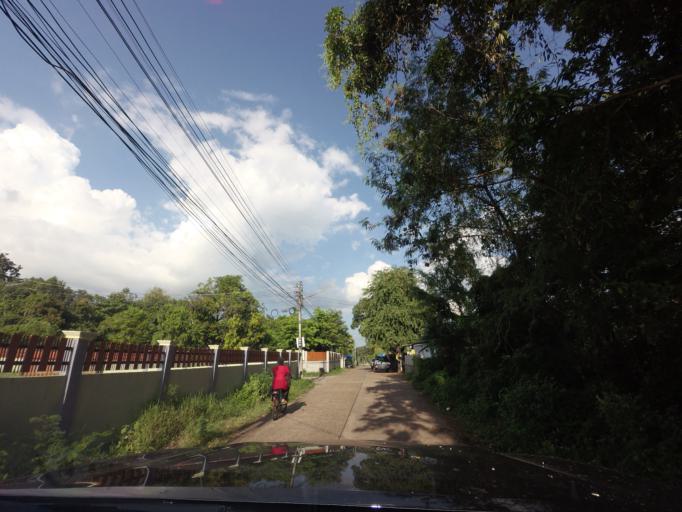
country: TH
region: Nong Khai
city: Nong Khai
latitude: 17.8868
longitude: 102.7791
